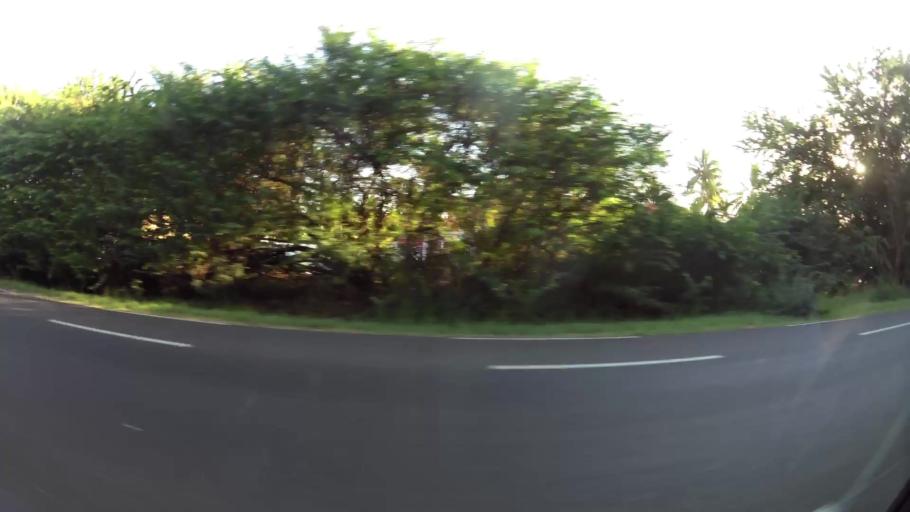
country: RE
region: Reunion
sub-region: Reunion
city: Trois-Bassins
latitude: -21.0873
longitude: 55.2332
